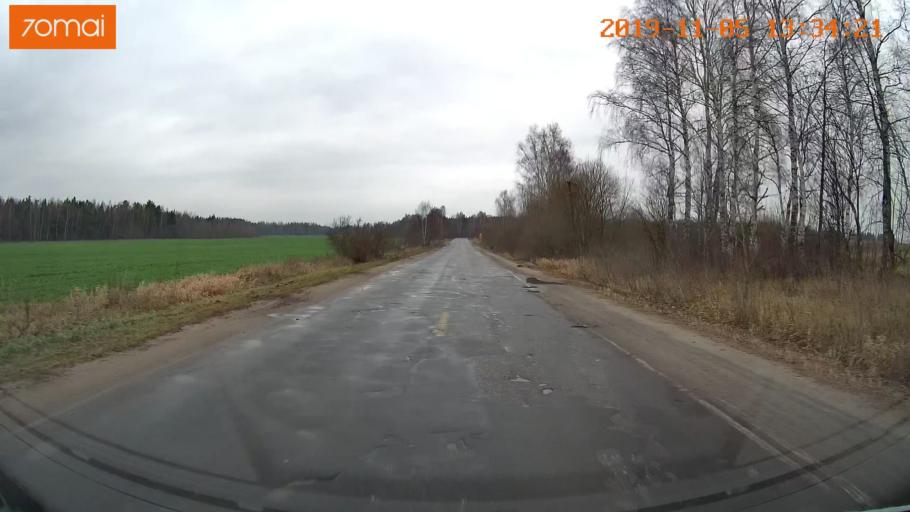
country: RU
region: Ivanovo
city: Shuya
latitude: 56.8998
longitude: 41.3900
